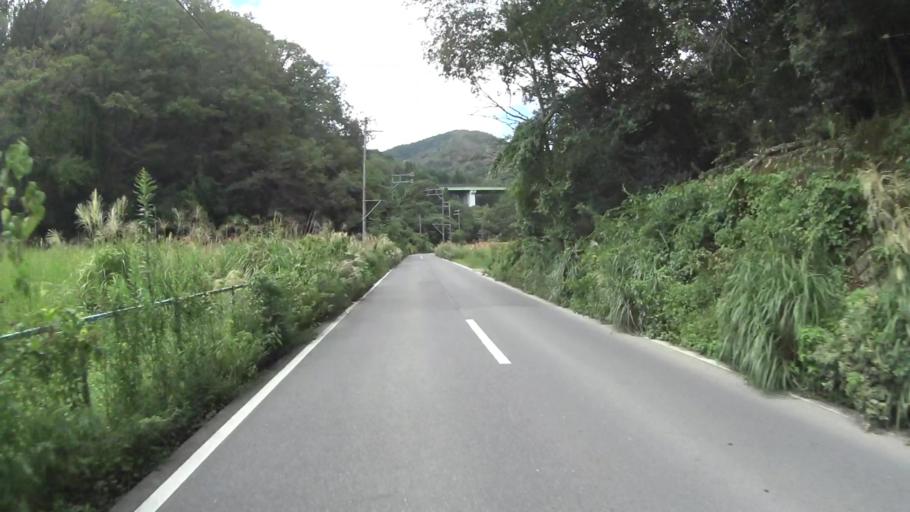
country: JP
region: Kyoto
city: Uji
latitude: 34.9182
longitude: 135.8857
